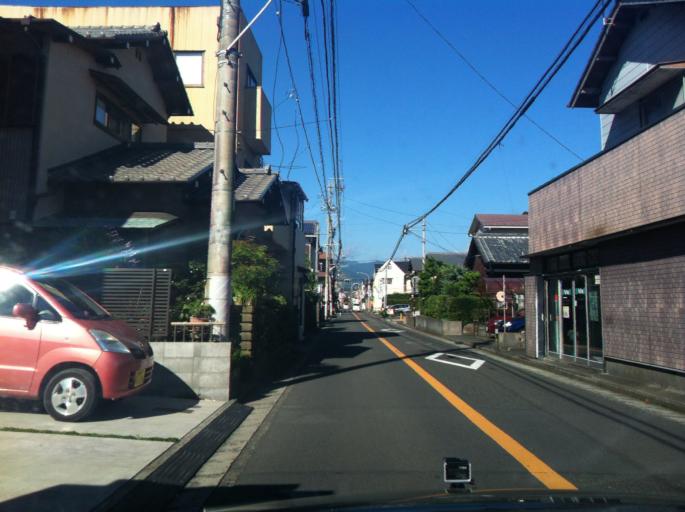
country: JP
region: Shizuoka
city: Shizuoka-shi
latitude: 34.9772
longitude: 138.4261
